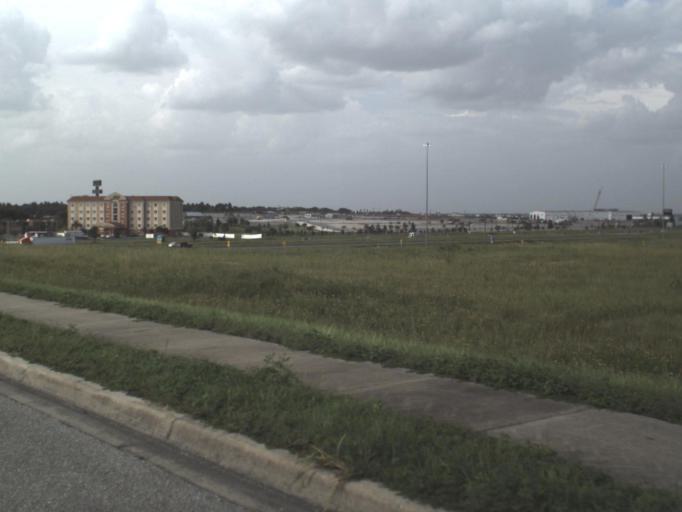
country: US
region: Florida
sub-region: Polk County
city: Loughman
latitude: 28.2305
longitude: -81.6485
